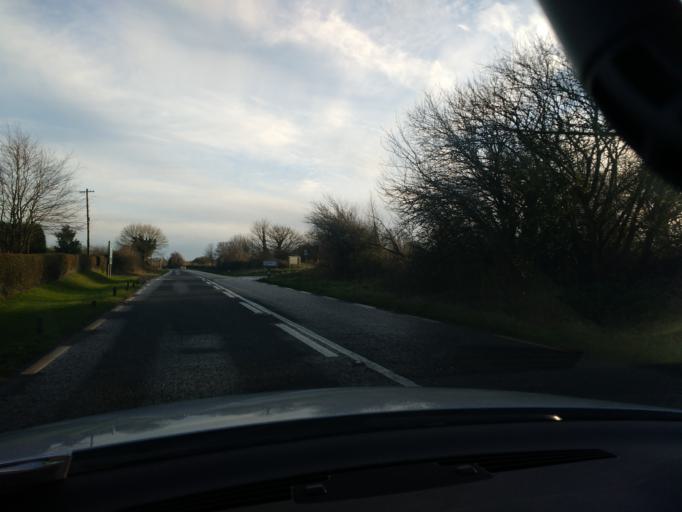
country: IE
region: Munster
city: Thurles
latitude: 52.6410
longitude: -7.7864
